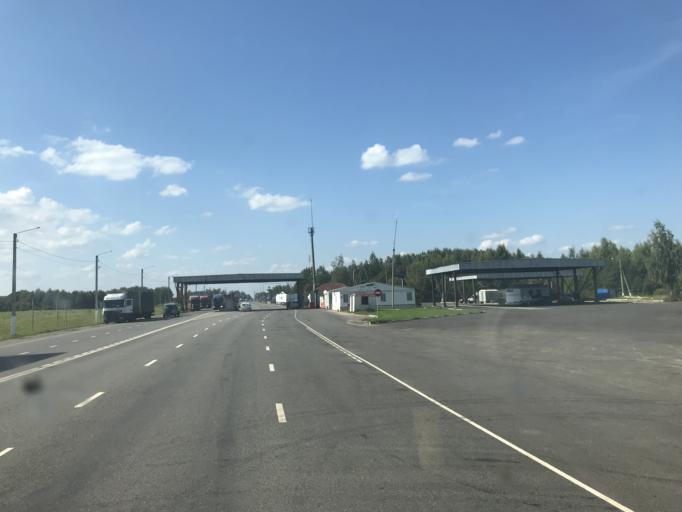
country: RU
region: Smolensk
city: Rudnya
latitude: 54.9876
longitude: 30.9570
